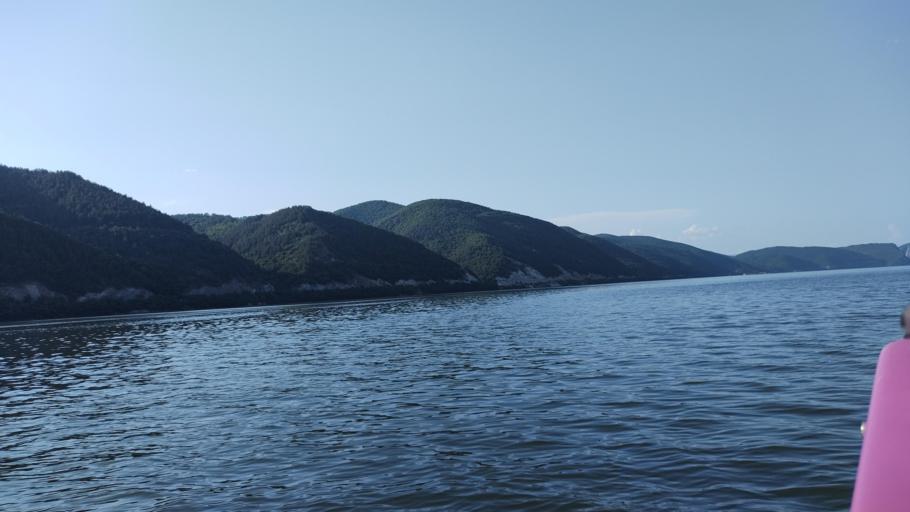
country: RO
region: Mehedinti
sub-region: Comuna Dubova
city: Dubova
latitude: 44.5305
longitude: 22.2123
